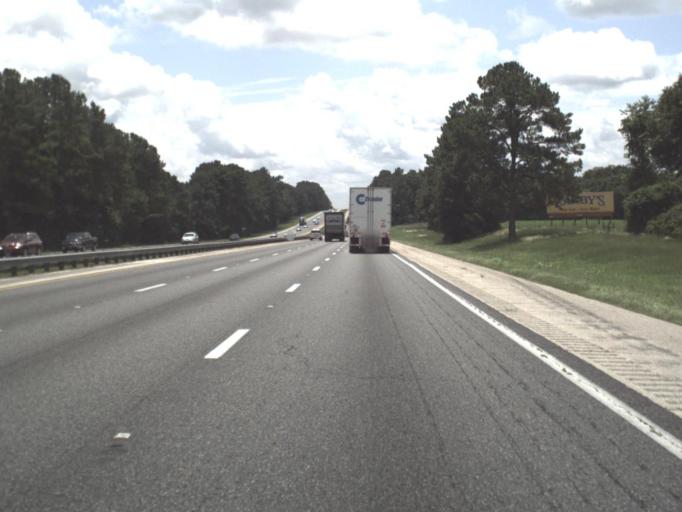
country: US
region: Florida
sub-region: Alachua County
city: High Springs
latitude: 29.8277
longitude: -82.5219
